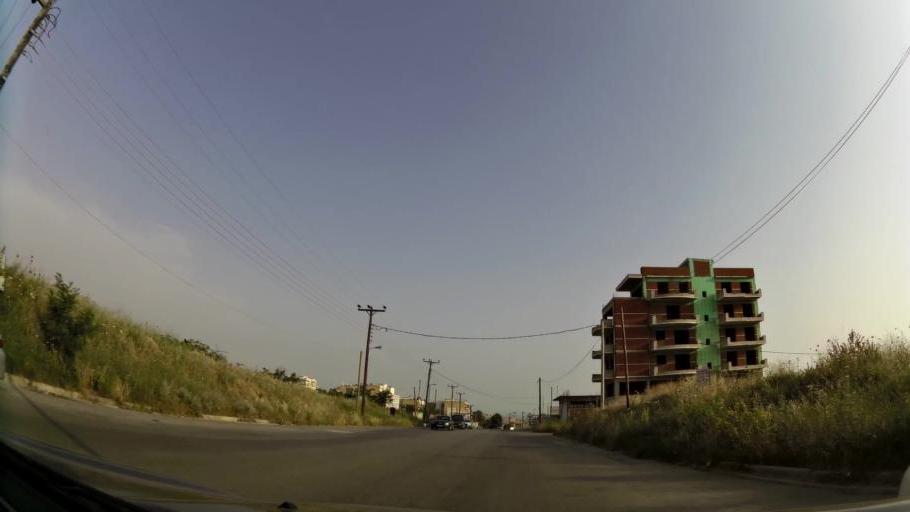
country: GR
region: Central Macedonia
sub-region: Nomos Thessalonikis
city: Evosmos
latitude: 40.6819
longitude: 22.9064
